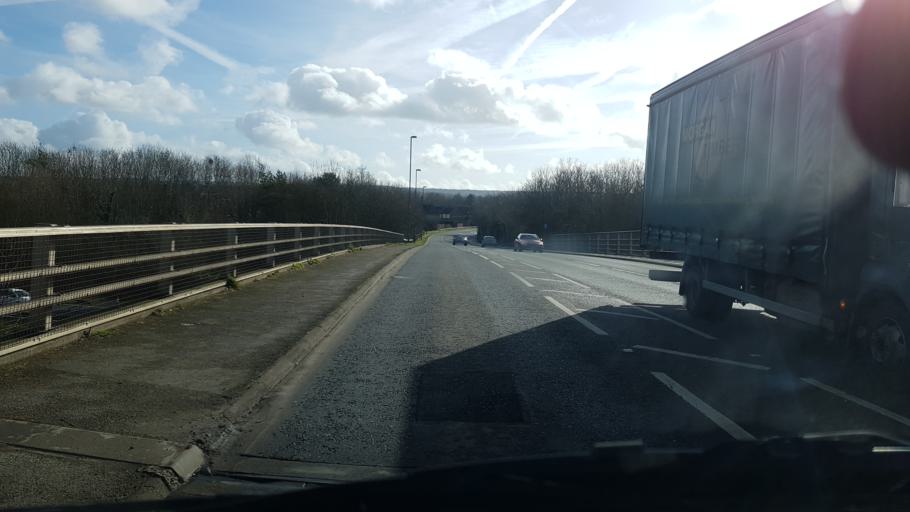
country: GB
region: England
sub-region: Surrey
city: Send
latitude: 51.2645
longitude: -0.5505
